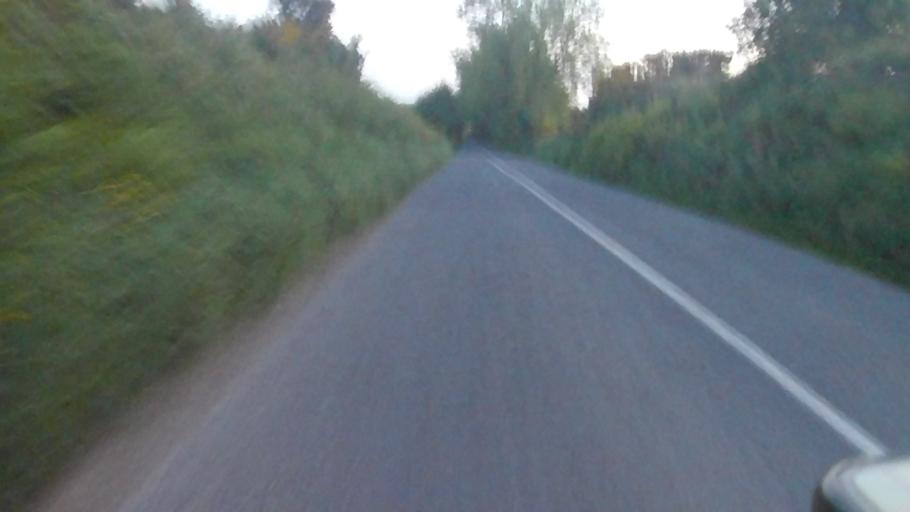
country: IE
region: Munster
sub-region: County Cork
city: Carrigtwohill
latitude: 51.9474
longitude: -8.3037
